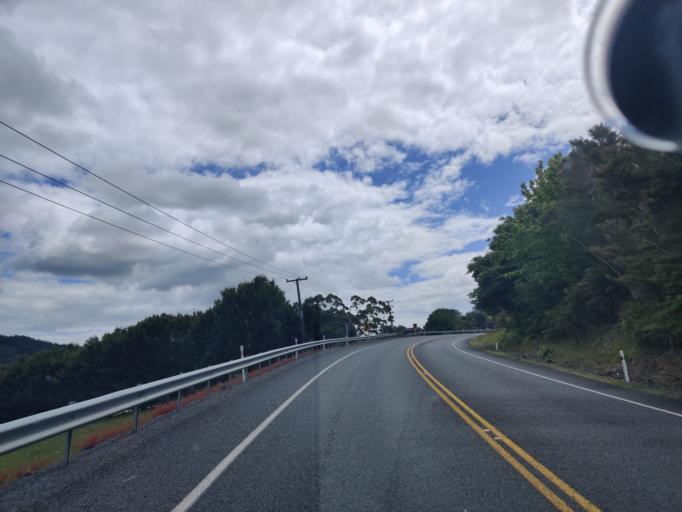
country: NZ
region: Northland
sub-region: Far North District
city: Paihia
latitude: -35.2915
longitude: 174.0101
